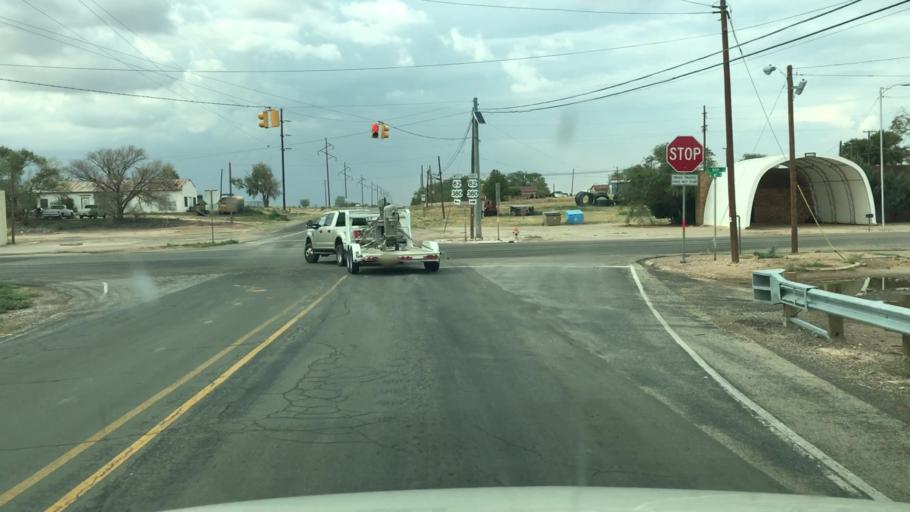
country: US
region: Texas
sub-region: Terry County
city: Brownfield
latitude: 33.1787
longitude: -102.2915
